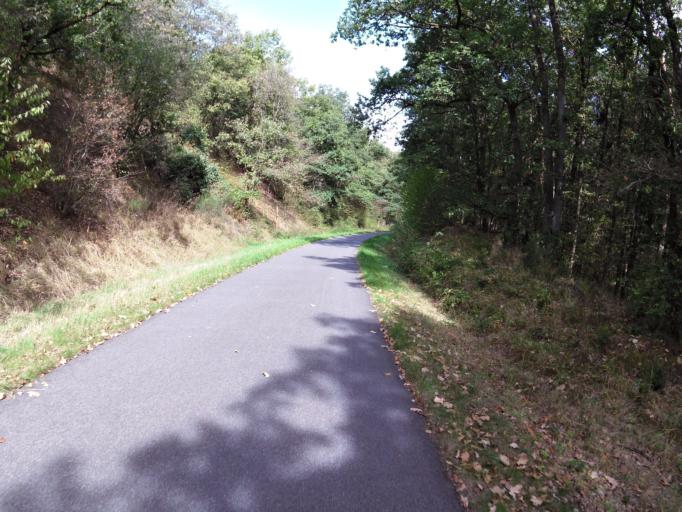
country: DE
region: Rheinland-Pfalz
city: Euscheid
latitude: 50.1278
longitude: 6.3027
